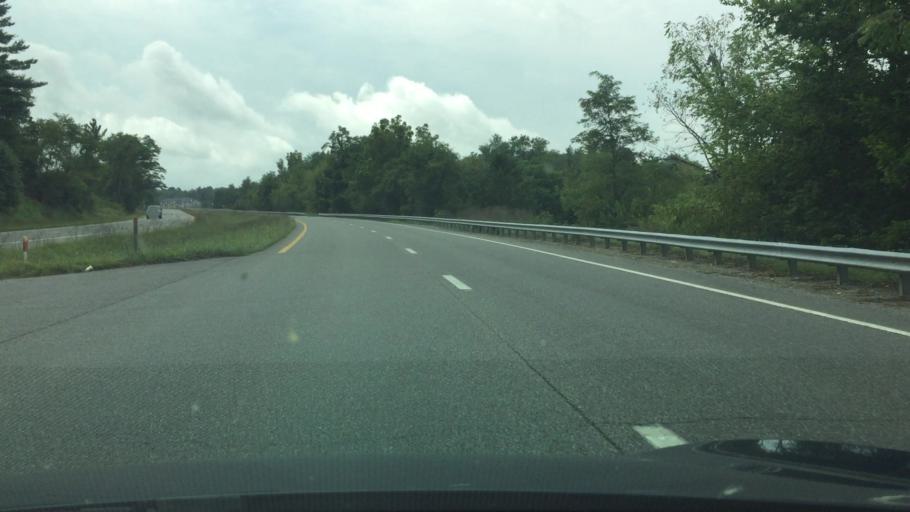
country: US
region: Virginia
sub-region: City of Radford
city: Radford
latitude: 37.1065
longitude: -80.5205
